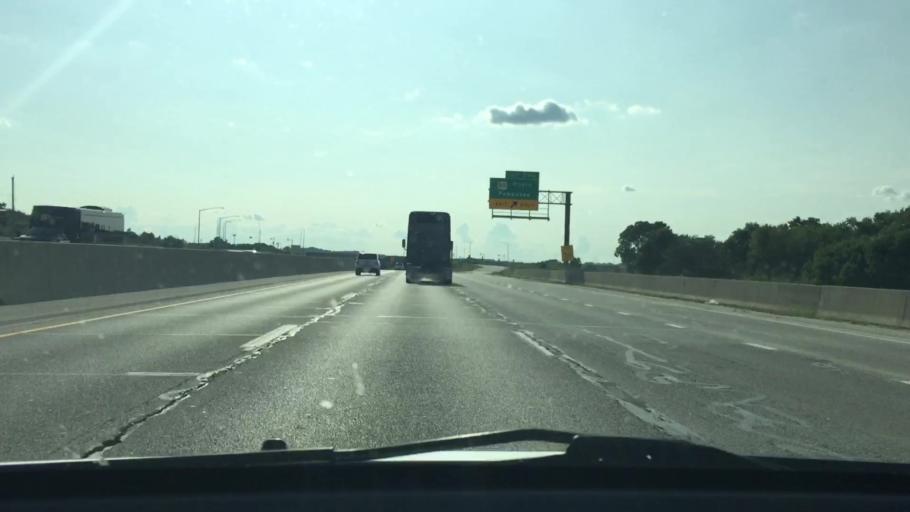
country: US
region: Wisconsin
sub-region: Waukesha County
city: Pewaukee
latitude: 43.0506
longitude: -88.2977
